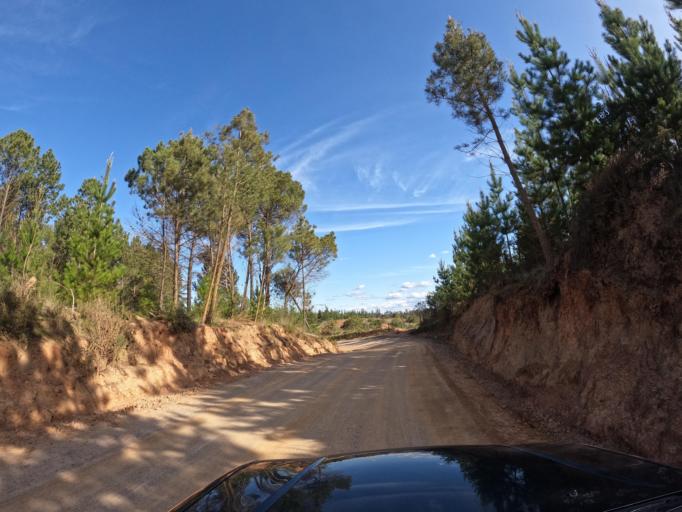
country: CL
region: Biobio
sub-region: Provincia de Biobio
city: La Laja
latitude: -37.1105
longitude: -72.7406
